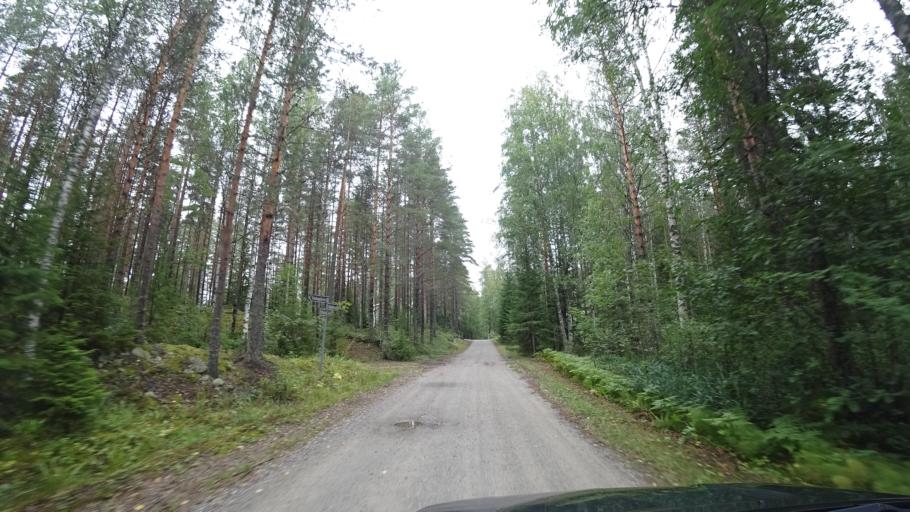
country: FI
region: Paijanne Tavastia
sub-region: Lahti
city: Auttoinen
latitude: 61.2206
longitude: 25.1415
